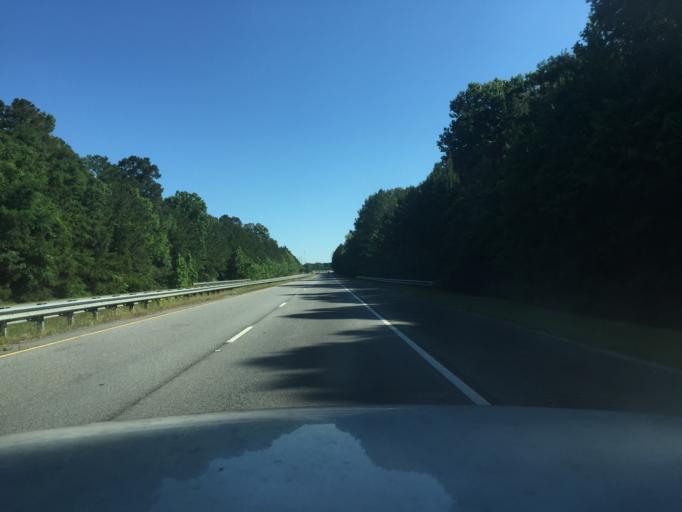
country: US
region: Georgia
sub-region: Chatham County
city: Georgetown
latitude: 32.0302
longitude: -81.1681
